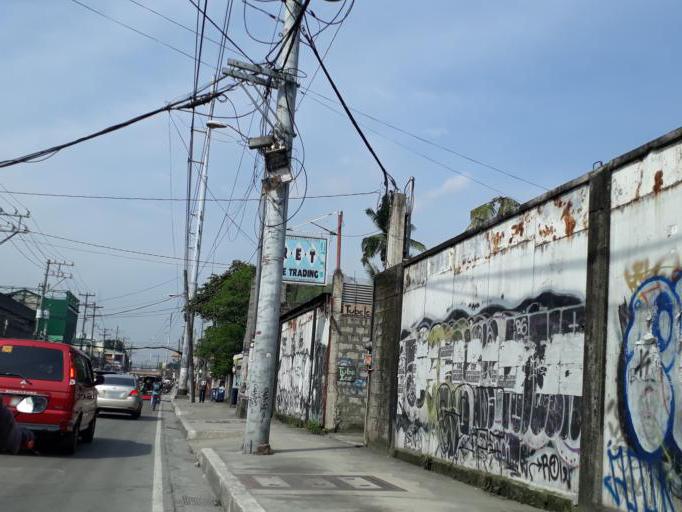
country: PH
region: Calabarzon
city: Bagong Pagasa
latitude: 14.6898
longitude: 121.0271
